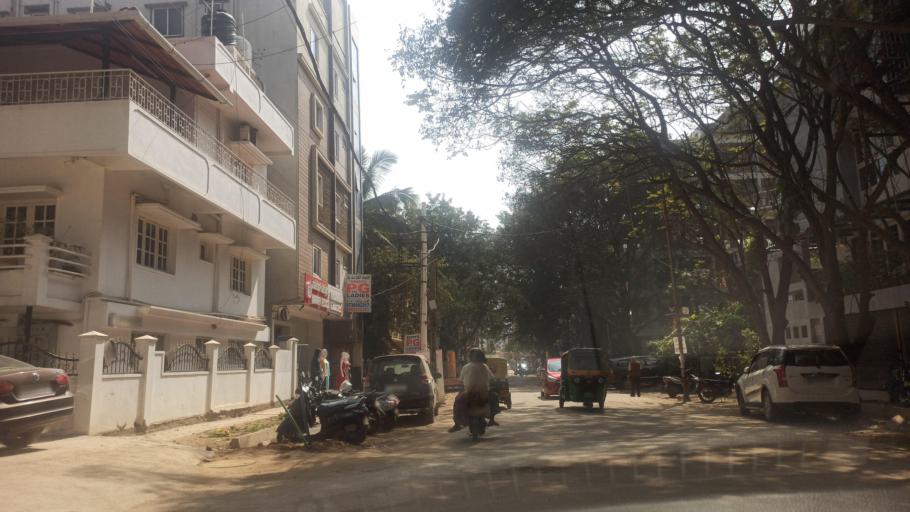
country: IN
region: Karnataka
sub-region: Bangalore Urban
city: Bangalore
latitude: 12.9618
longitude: 77.7135
